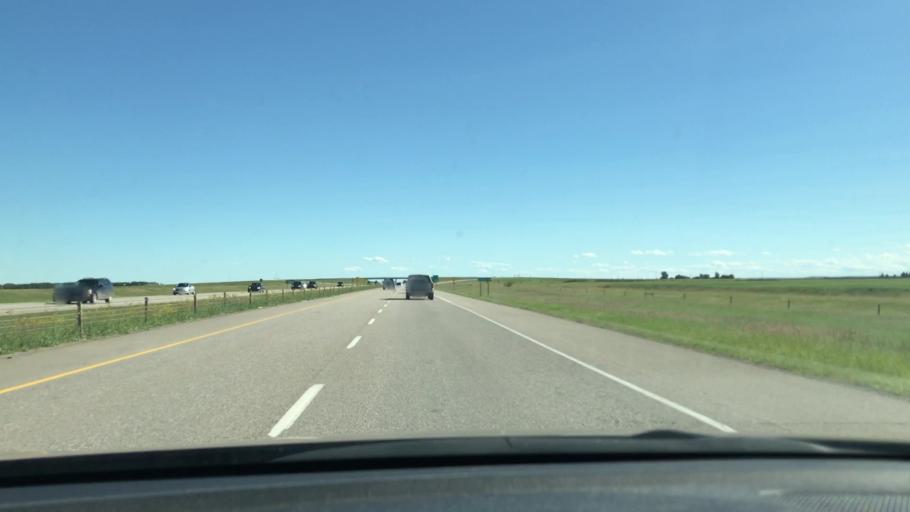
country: CA
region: Alberta
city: Didsbury
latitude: 51.6737
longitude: -114.0256
